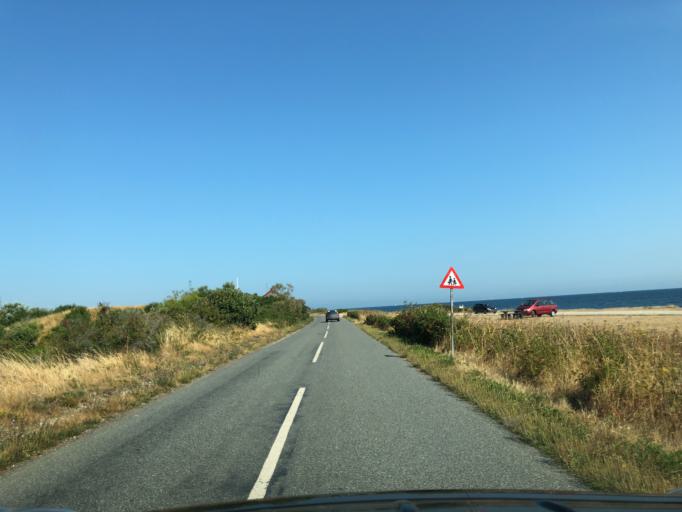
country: DK
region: Zealand
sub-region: Odsherred Kommune
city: Asnaes
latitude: 55.9998
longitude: 11.2877
